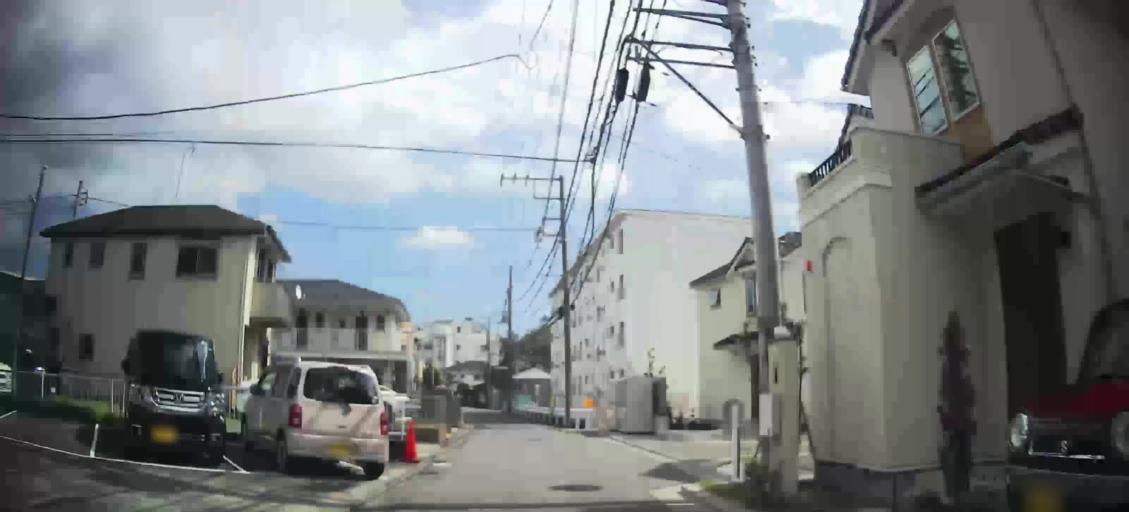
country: JP
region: Kanagawa
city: Yokohama
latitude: 35.4862
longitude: 139.5508
